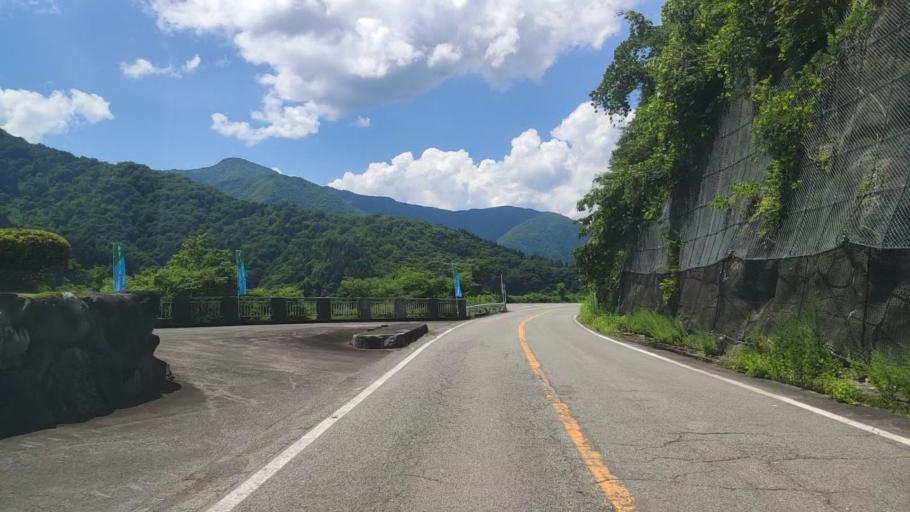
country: JP
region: Fukui
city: Ono
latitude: 35.9178
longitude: 136.5396
